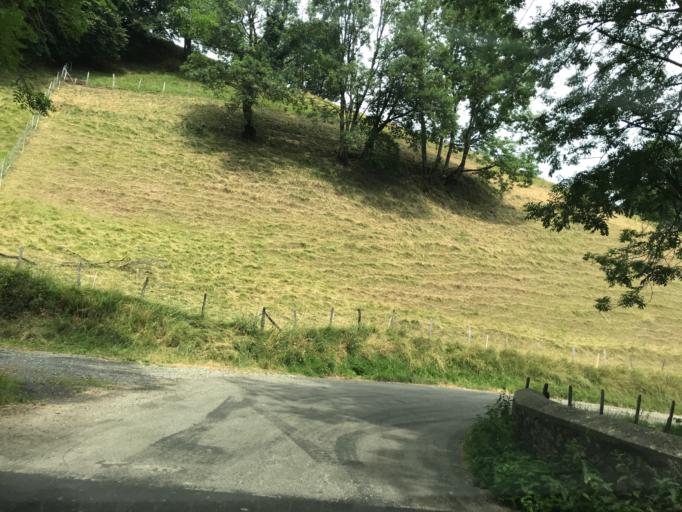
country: FR
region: Rhone-Alpes
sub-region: Departement de l'Isere
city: Barraux
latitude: 45.4498
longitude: 5.9633
